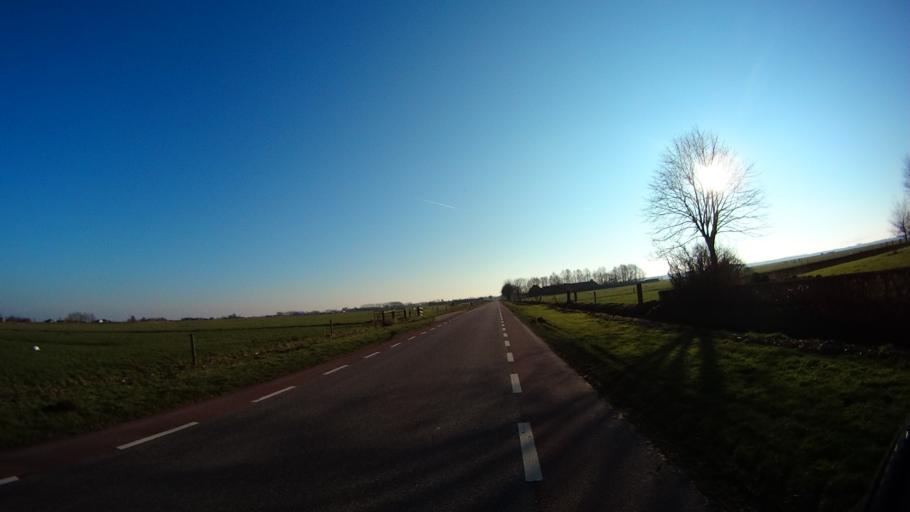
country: NL
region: Utrecht
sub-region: Gemeente Baarn
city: Baarn
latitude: 52.2430
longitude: 5.3020
